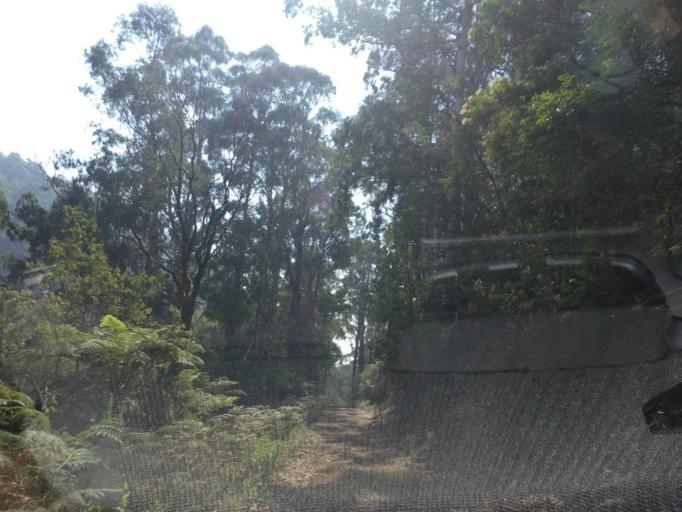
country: AU
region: Victoria
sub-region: Yarra Ranges
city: Healesville
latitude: -37.5659
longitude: 145.6189
